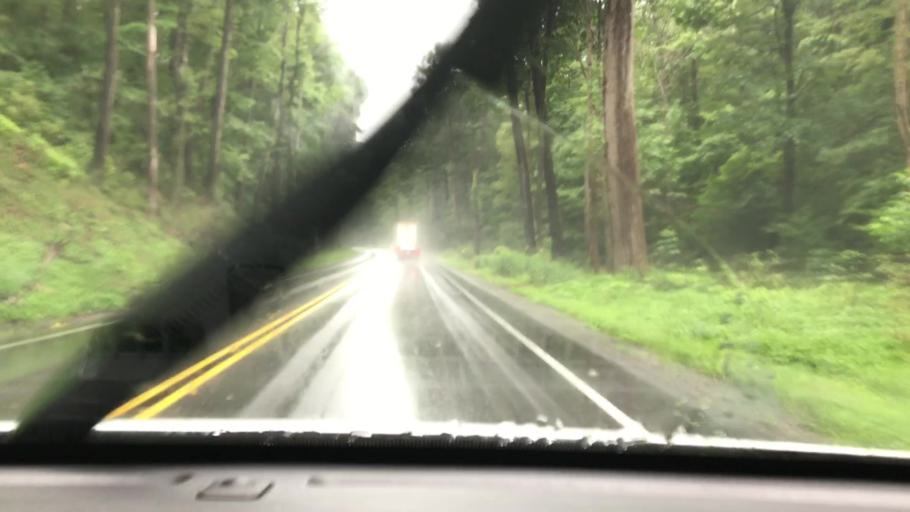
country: US
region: Pennsylvania
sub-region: Blair County
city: Tyrone
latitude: 40.7576
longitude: -78.2255
